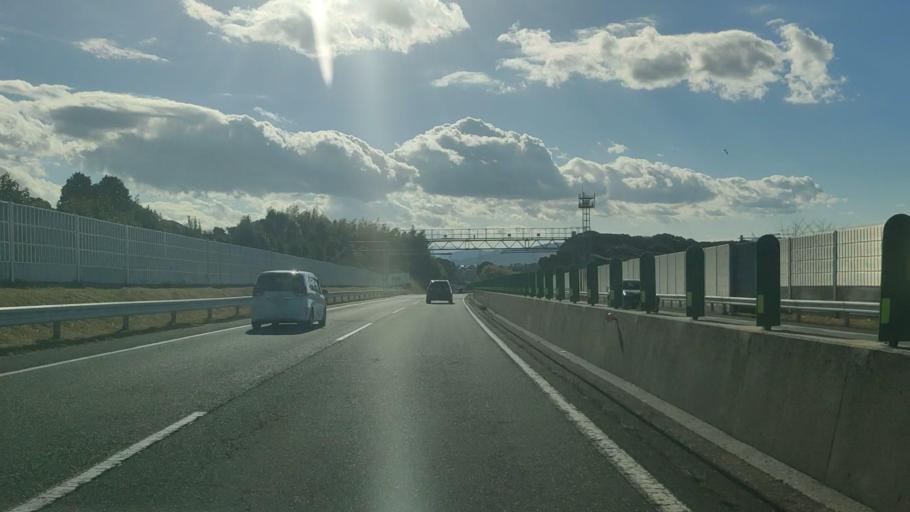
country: JP
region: Fukuoka
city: Nakama
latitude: 33.8252
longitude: 130.7631
